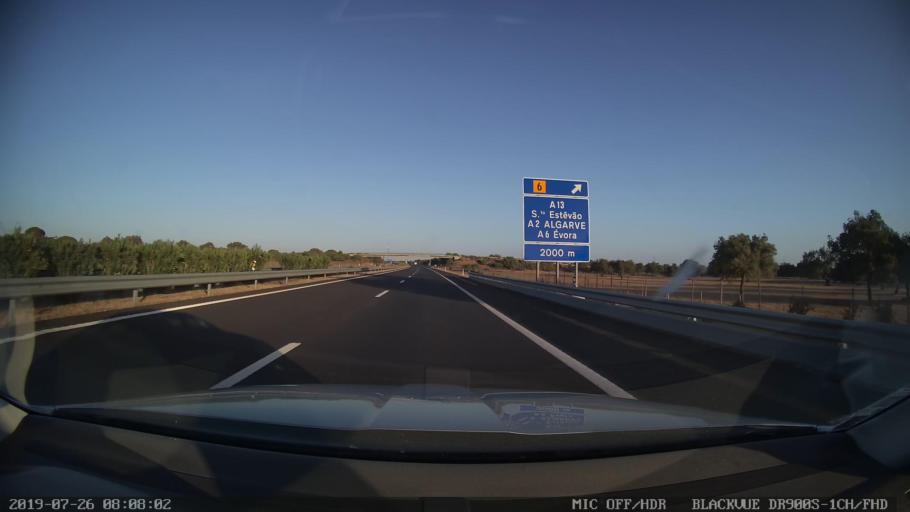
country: PT
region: Santarem
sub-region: Benavente
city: Benavente
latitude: 38.9260
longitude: -8.8137
